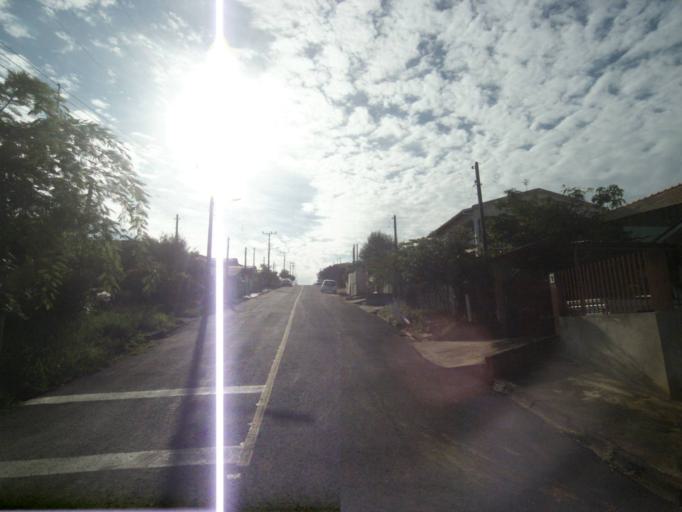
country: BR
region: Parana
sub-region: Telemaco Borba
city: Telemaco Borba
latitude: -24.3453
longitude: -50.6085
